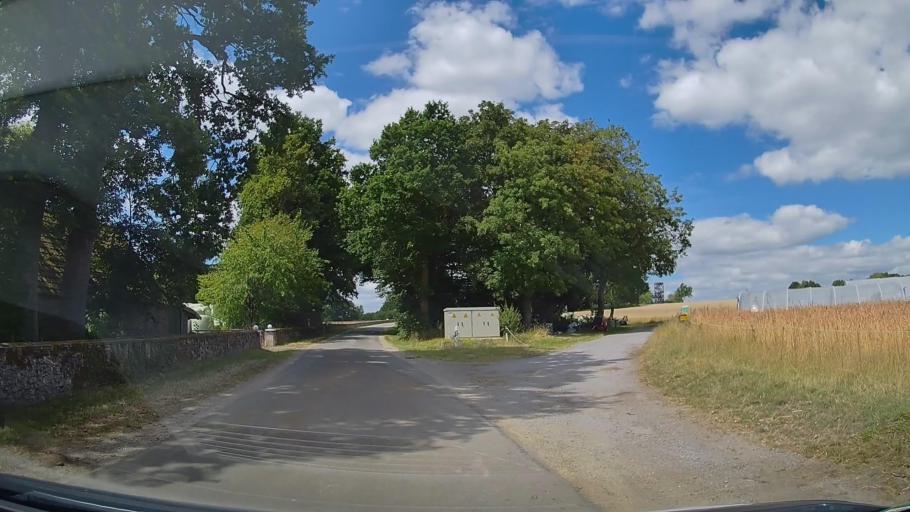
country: DE
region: Lower Saxony
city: Belm
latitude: 52.3870
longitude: 8.1337
